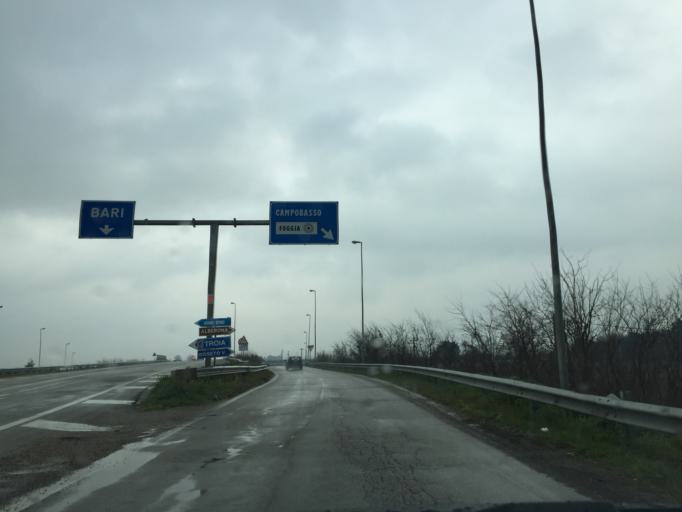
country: IT
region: Apulia
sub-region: Provincia di Foggia
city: Foggia
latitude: 41.4743
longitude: 15.5091
